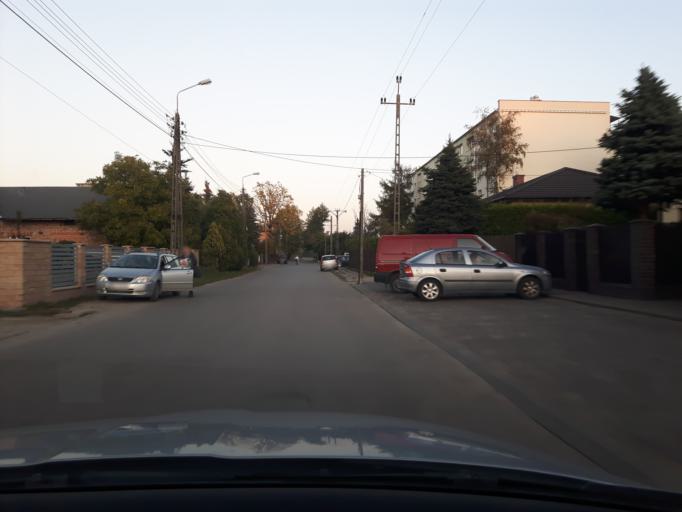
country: PL
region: Masovian Voivodeship
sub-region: Powiat wolominski
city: Kobylka
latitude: 52.3360
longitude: 21.1917
